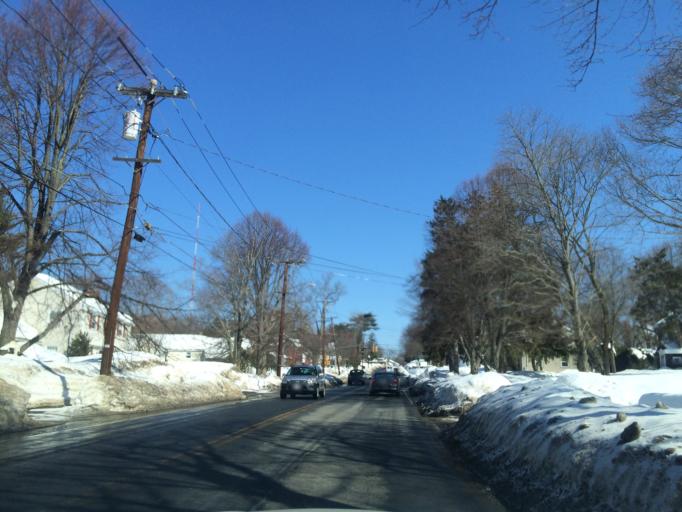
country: US
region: Massachusetts
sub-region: Norfolk County
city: Needham
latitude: 42.3012
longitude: -71.2455
